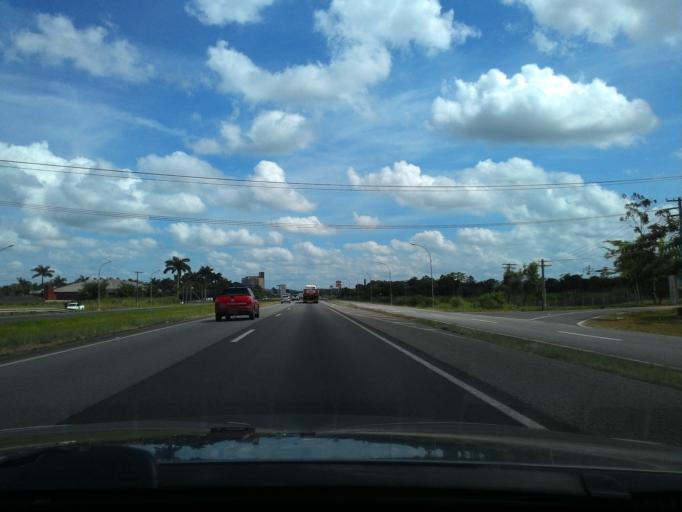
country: BR
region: Sao Paulo
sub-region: Registro
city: Registro
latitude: -24.5214
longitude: -47.8537
